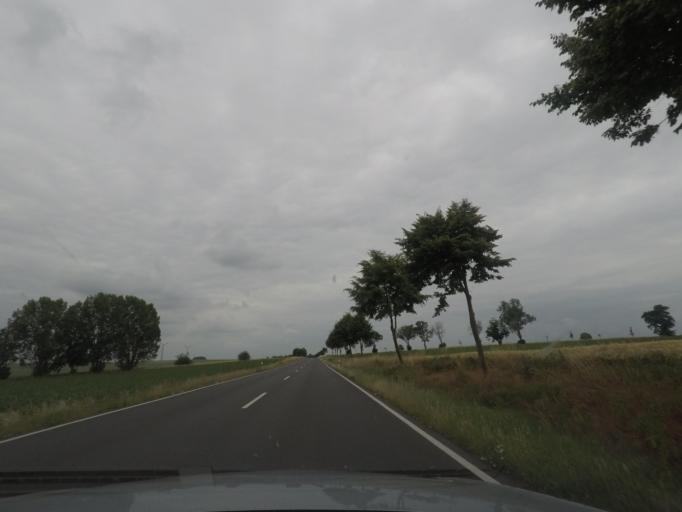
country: DE
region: Saxony-Anhalt
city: Erxleben
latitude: 52.2087
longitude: 11.2846
